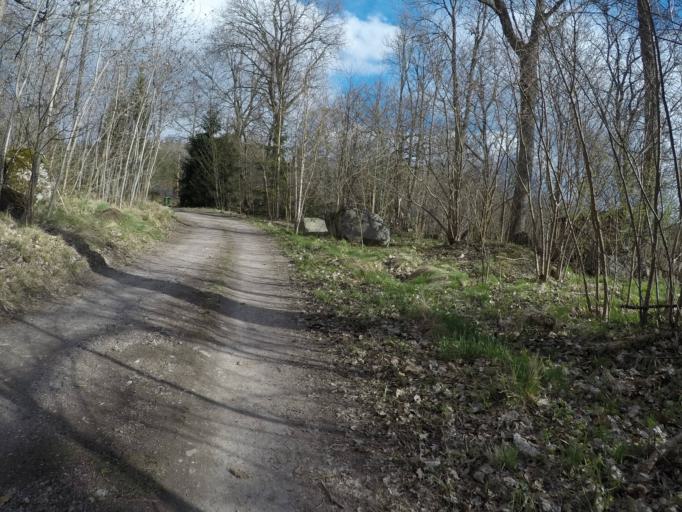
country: SE
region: Soedermanland
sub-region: Eskilstuna Kommun
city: Kvicksund
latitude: 59.4725
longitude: 16.2964
